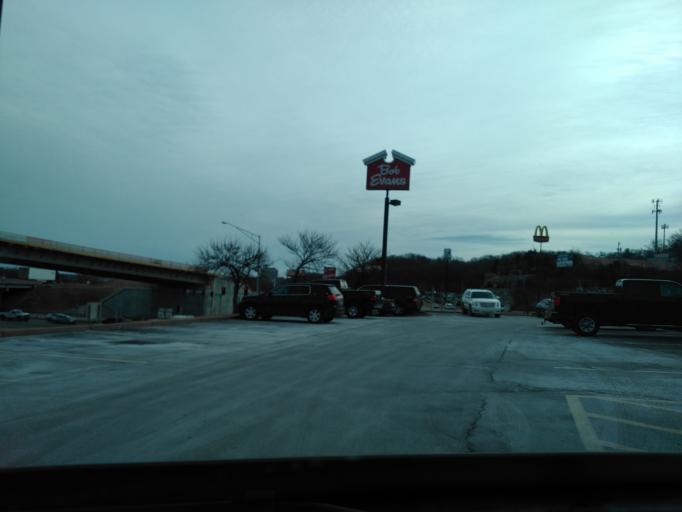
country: US
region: Missouri
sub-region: Saint Louis County
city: Valley Park
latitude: 38.5381
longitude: -90.4968
